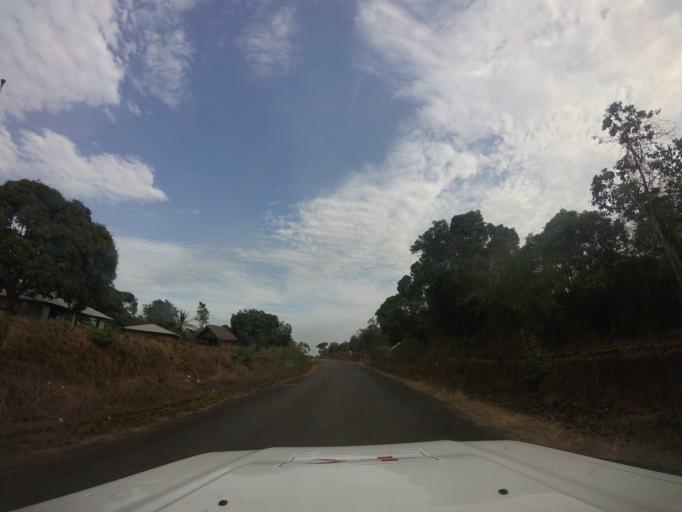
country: LR
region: Grand Cape Mount
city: Robertsport
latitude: 6.9144
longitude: -11.2444
